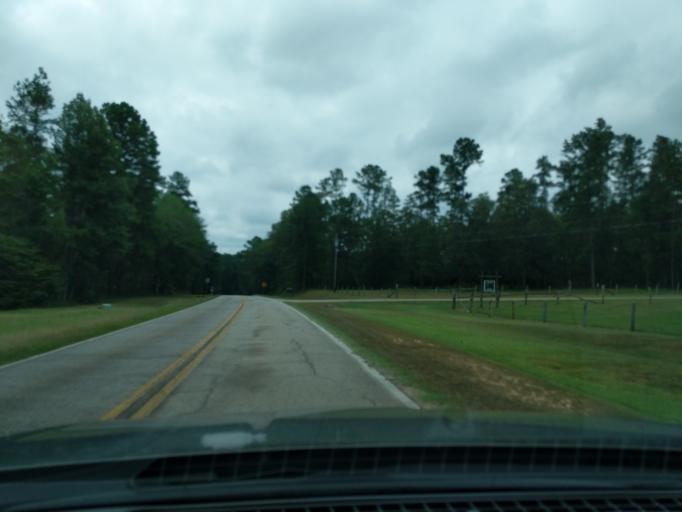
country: US
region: Georgia
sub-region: Columbia County
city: Appling
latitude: 33.5763
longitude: -82.3691
